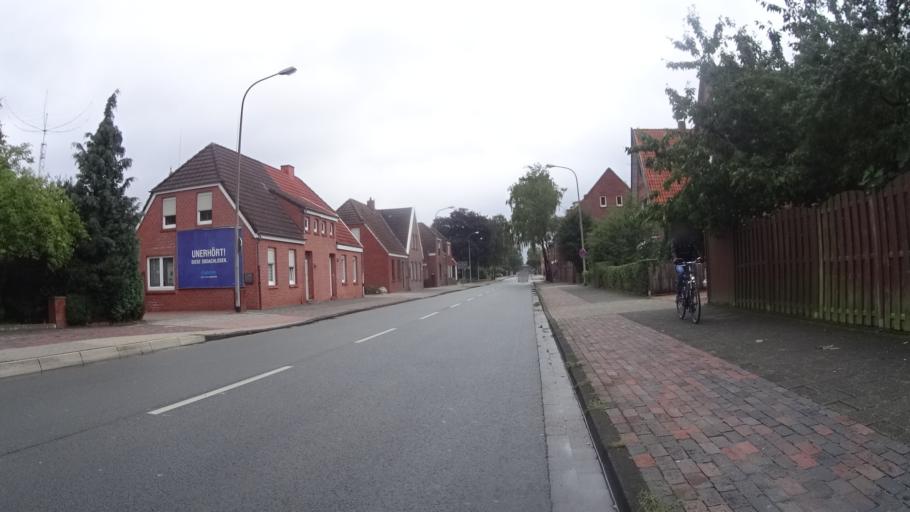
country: DE
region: Lower Saxony
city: Leer
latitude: 53.2309
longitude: 7.4435
